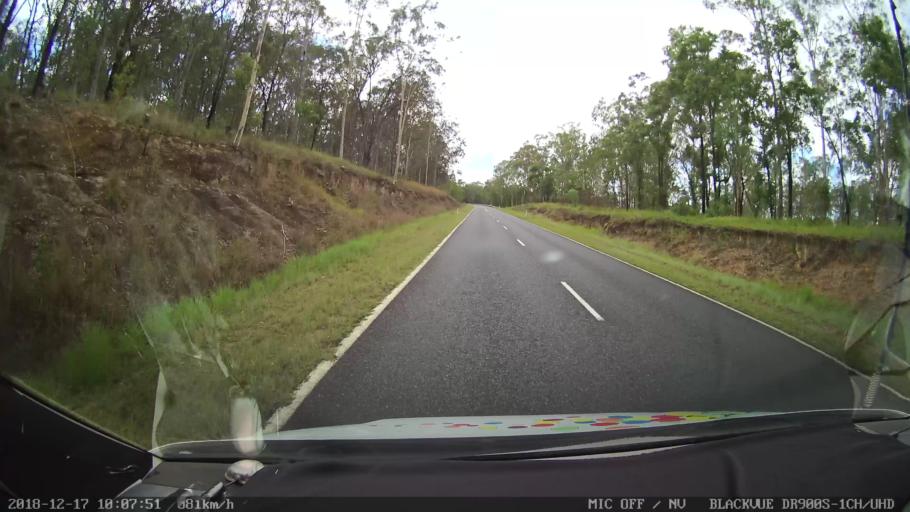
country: AU
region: New South Wales
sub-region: Tenterfield Municipality
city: Carrolls Creek
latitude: -28.8899
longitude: 152.5235
